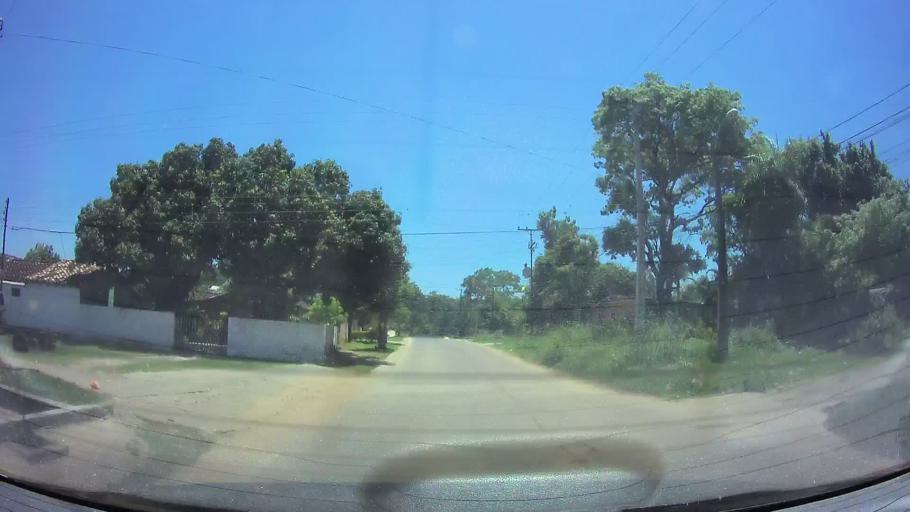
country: PY
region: Central
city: Fernando de la Mora
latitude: -25.2718
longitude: -57.5185
